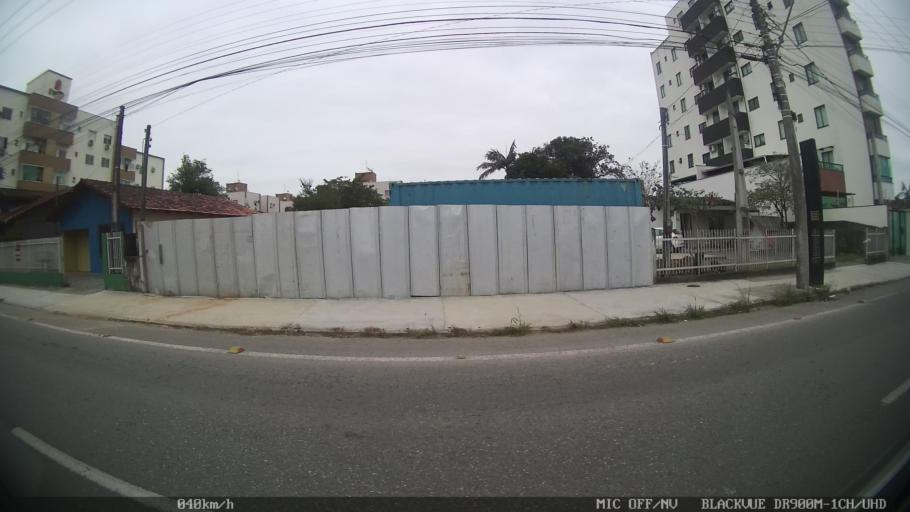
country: BR
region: Santa Catarina
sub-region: Joinville
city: Joinville
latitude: -26.3233
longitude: -48.8307
